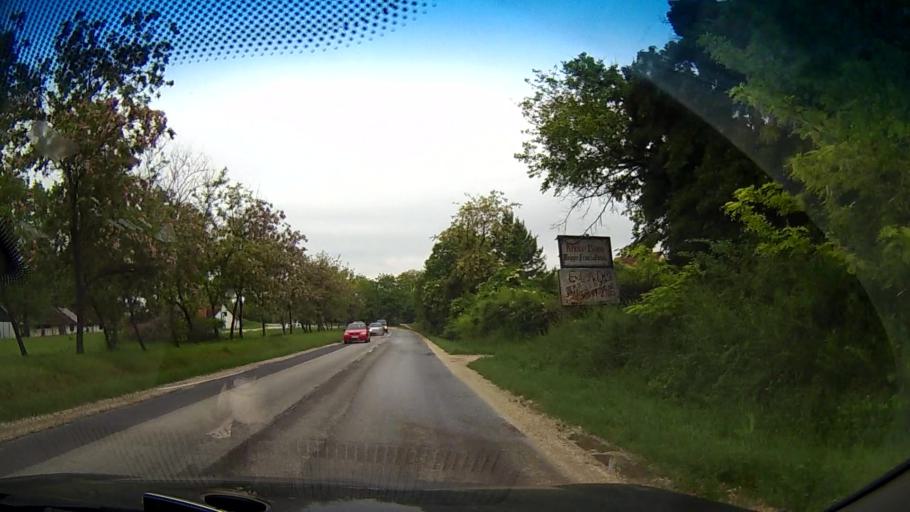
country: HU
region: Pest
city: Perbal
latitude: 47.5742
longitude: 18.7384
